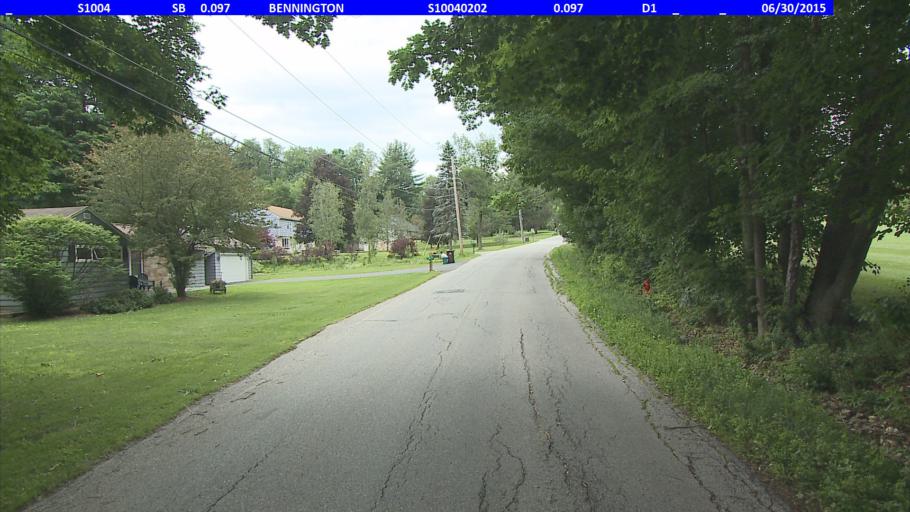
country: US
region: Vermont
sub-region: Bennington County
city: Bennington
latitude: 42.8912
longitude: -73.2062
